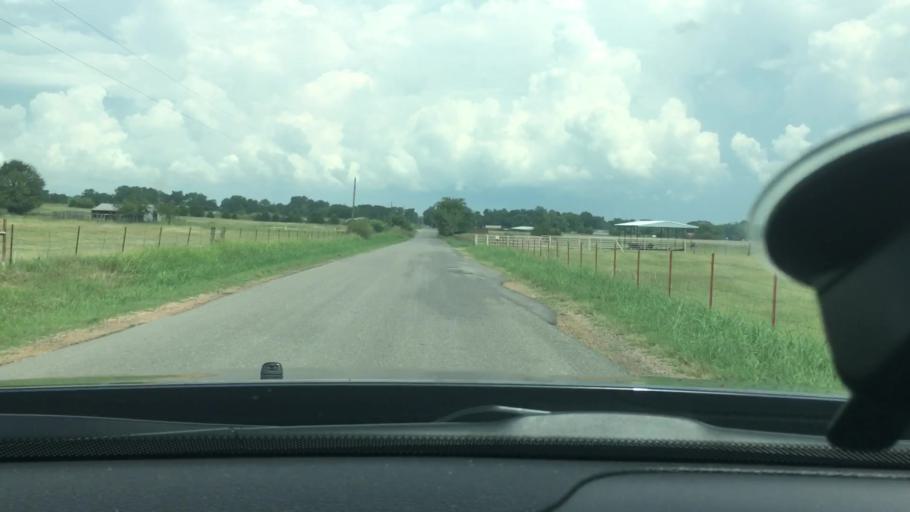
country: US
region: Oklahoma
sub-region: Carter County
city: Dickson
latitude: 34.1952
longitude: -96.8982
